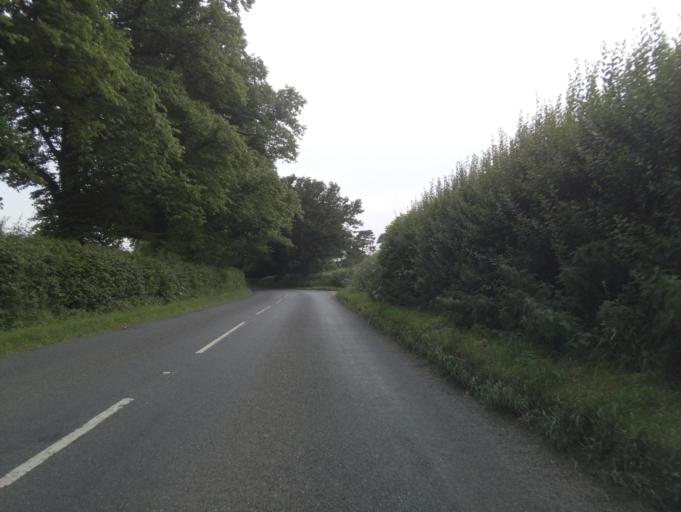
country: GB
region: England
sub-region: Somerset
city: Crewkerne
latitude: 50.8755
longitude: -2.7597
